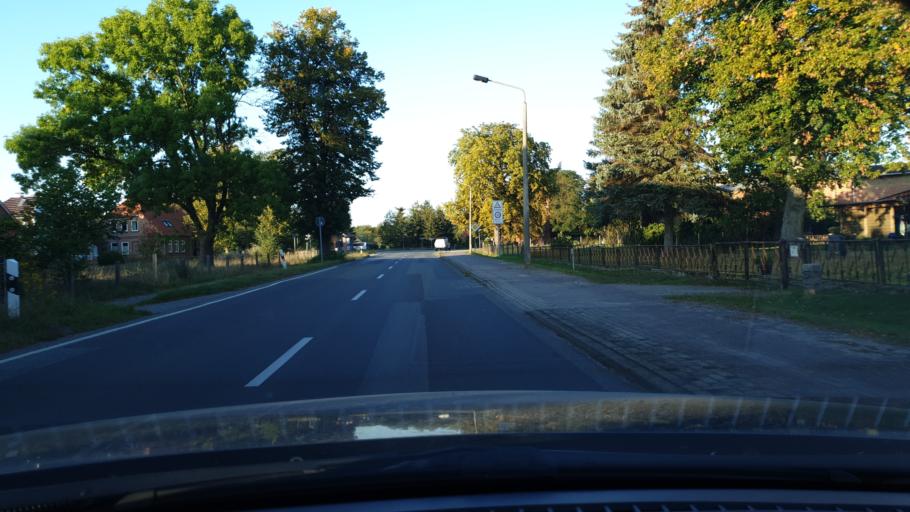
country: DE
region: Mecklenburg-Vorpommern
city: Wittenburg
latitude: 53.5384
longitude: 11.0821
